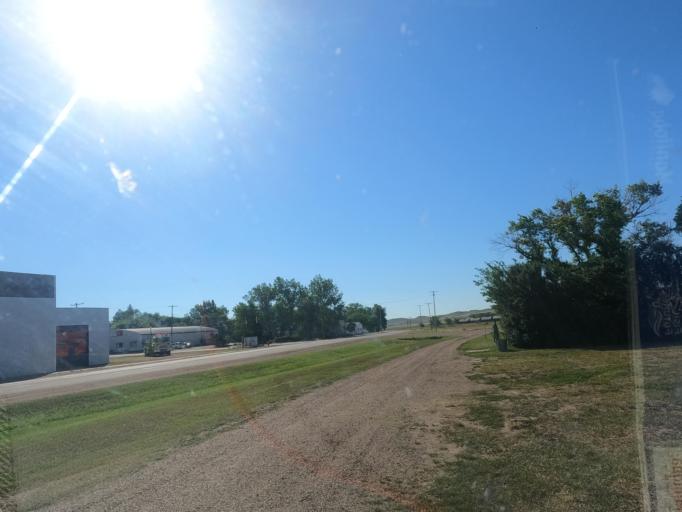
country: CA
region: Saskatchewan
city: Assiniboia
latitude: 49.1786
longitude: -105.9503
